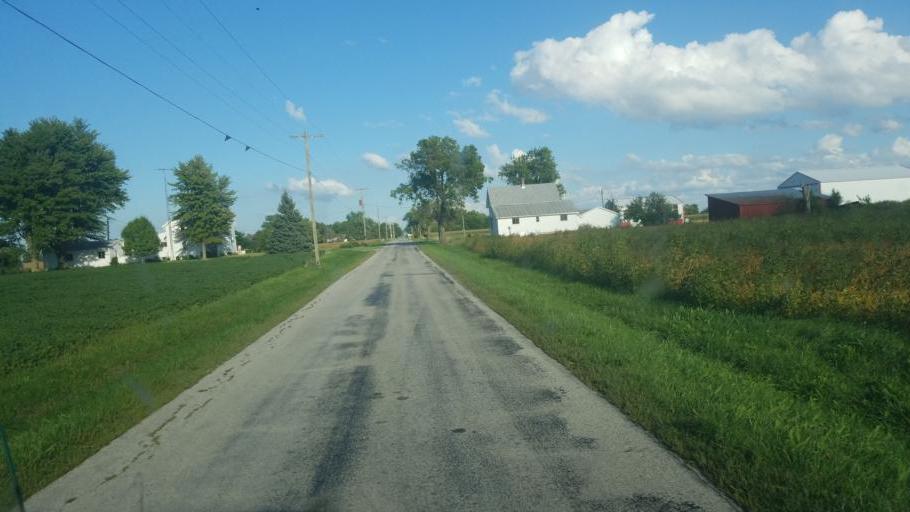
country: US
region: Ohio
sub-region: Hancock County
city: Arlington
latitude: 40.9355
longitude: -83.6031
